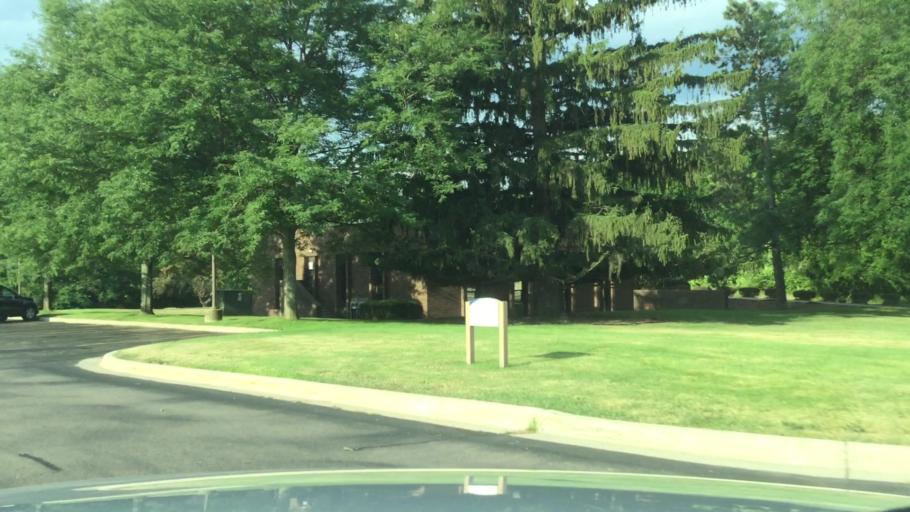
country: US
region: Michigan
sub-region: Genesee County
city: Flushing
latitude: 43.0604
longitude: -83.7766
